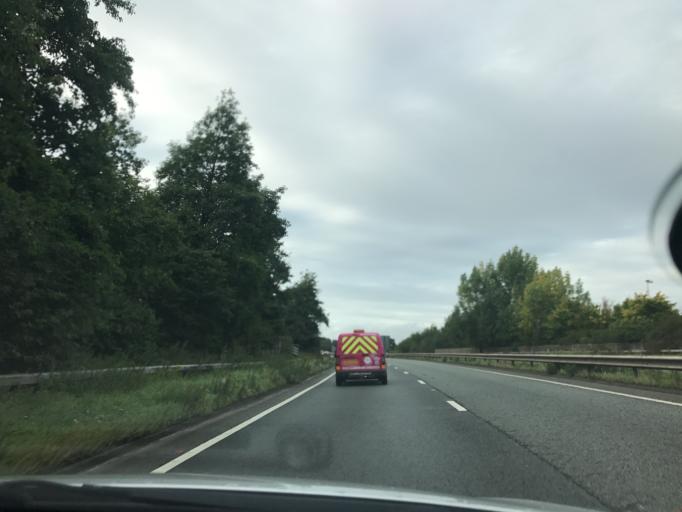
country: GB
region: England
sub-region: Cheshire West and Chester
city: Guilden Sutton
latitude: 53.2051
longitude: -2.8439
